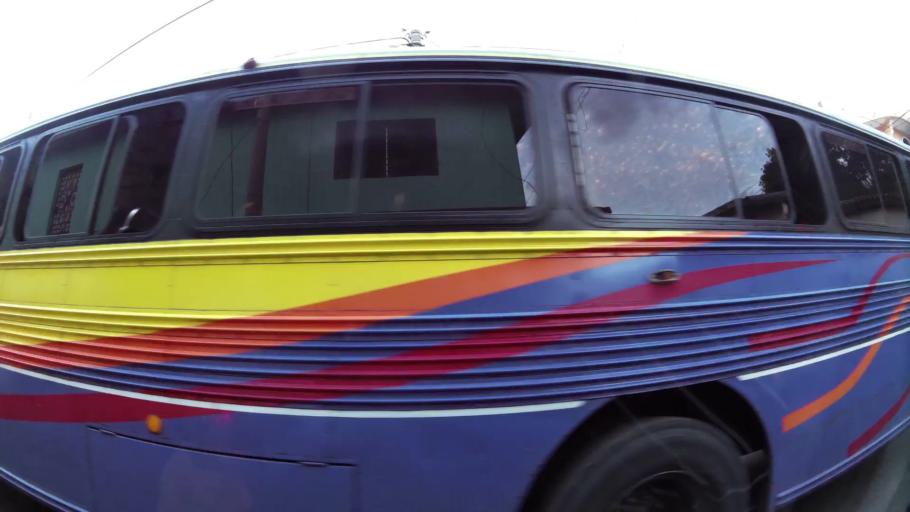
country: SV
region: San Vicente
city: San Vicente
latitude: 13.6441
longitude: -88.7891
